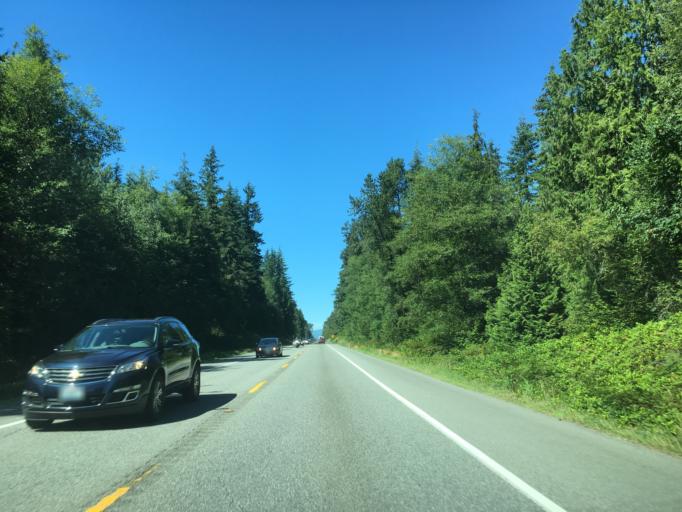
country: US
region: Washington
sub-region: Snohomish County
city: Sisco Heights
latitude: 48.1100
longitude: -122.1123
